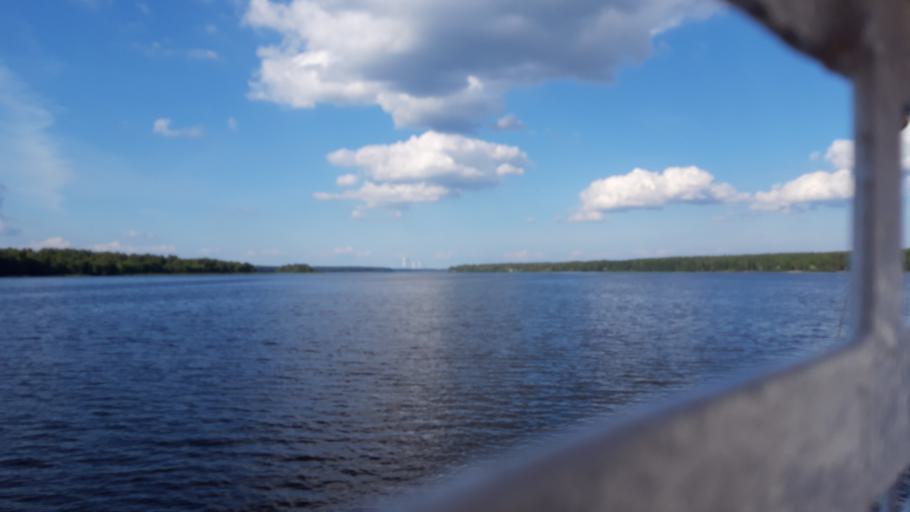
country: RU
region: Tverskaya
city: Konakovo
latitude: 56.6698
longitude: 36.6647
